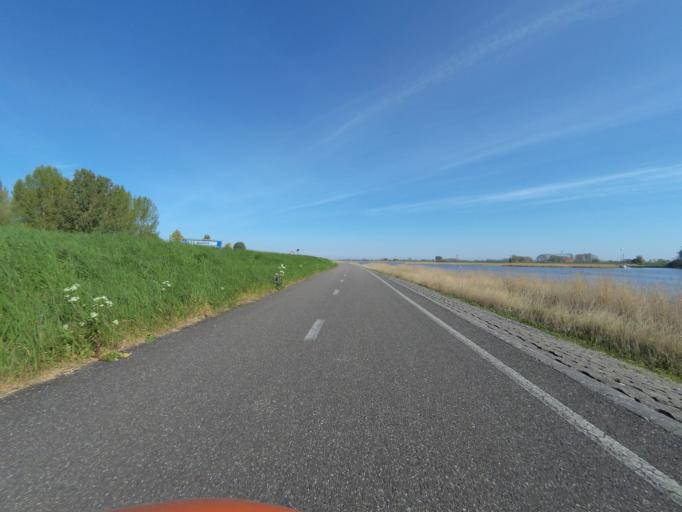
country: NL
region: Overijssel
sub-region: Gemeente Kampen
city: Kampen
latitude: 52.5487
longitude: 5.8533
